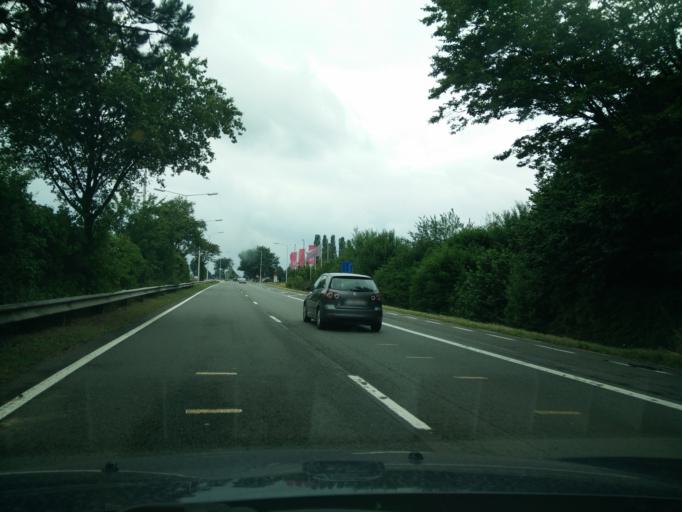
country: BE
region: Flanders
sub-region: Provincie Oost-Vlaanderen
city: Oudenaarde
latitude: 50.8697
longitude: 3.6071
